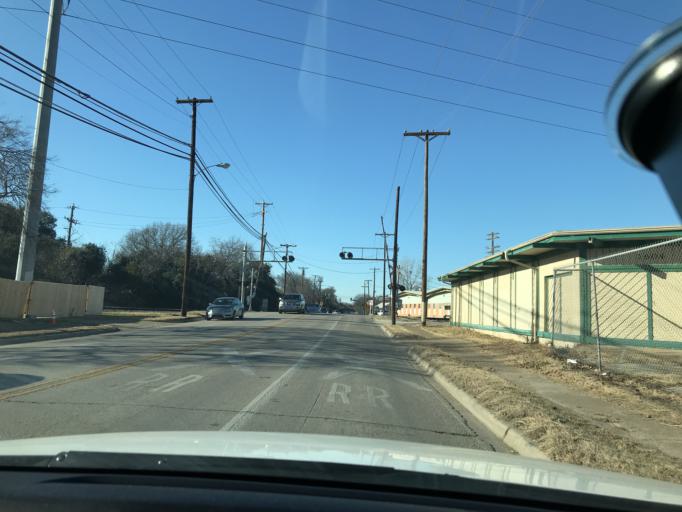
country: US
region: Texas
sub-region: Dallas County
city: Garland
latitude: 32.8327
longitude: -96.6899
